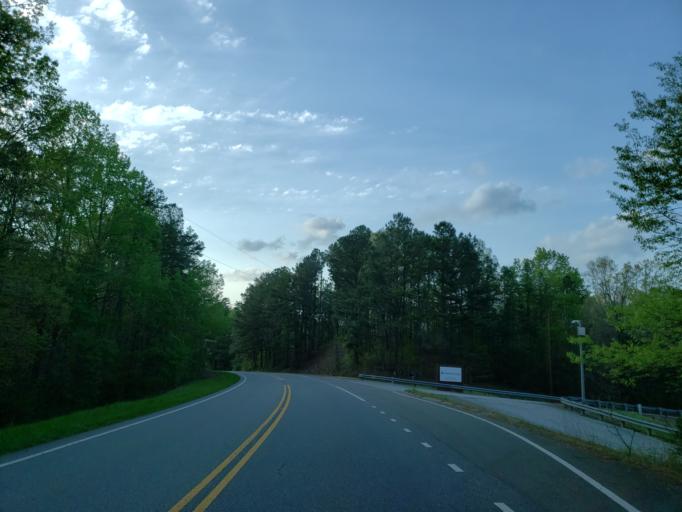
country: US
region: Georgia
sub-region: Cherokee County
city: Ball Ground
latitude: 34.2755
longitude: -84.3724
